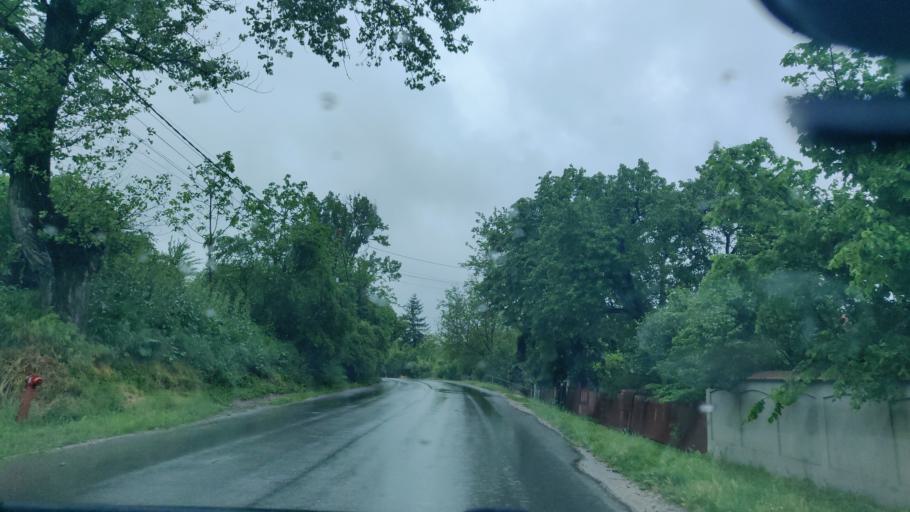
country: RO
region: Giurgiu
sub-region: Comuna Bulbucata
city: Bulbucata
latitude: 44.2877
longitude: 25.7971
